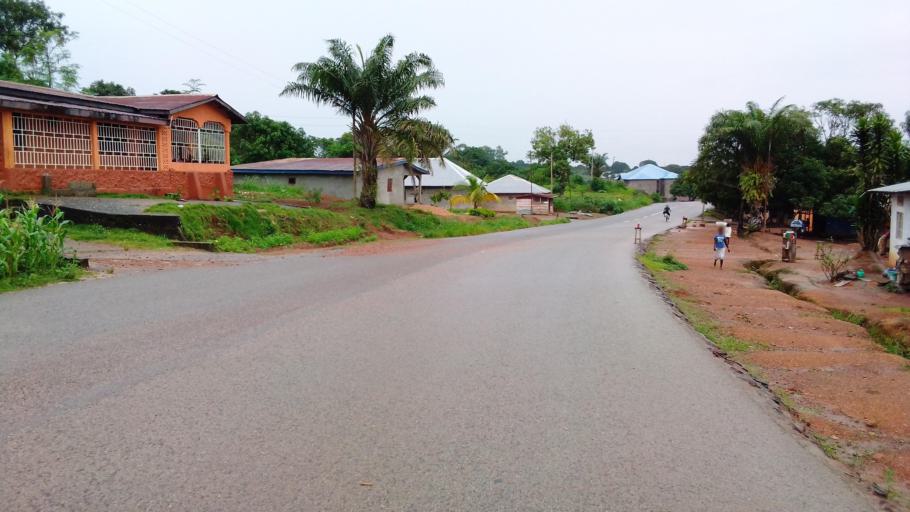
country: SL
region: Eastern Province
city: Kenema
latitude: 7.8775
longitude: -11.1697
